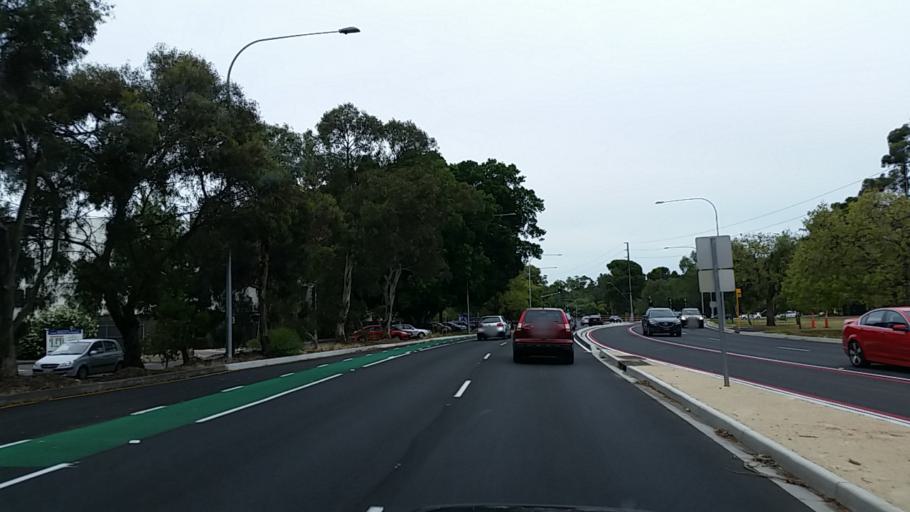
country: AU
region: South Australia
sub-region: Adelaide
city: North Adelaide
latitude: -34.9073
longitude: 138.6128
